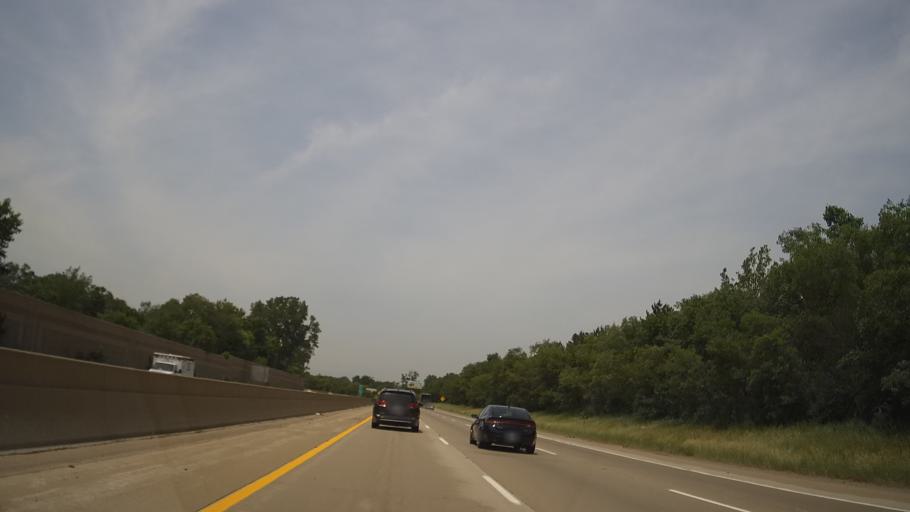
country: US
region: Michigan
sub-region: Washtenaw County
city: Ypsilanti
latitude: 42.2279
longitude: -83.5728
